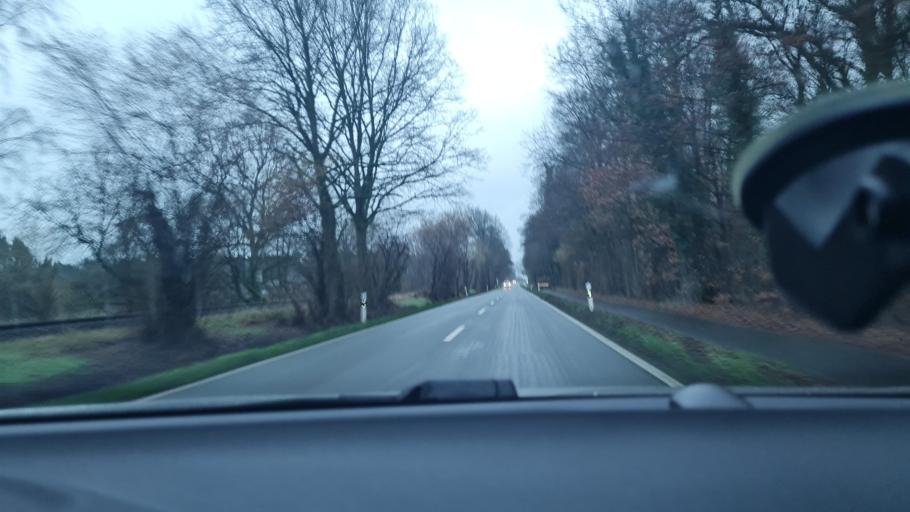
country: DE
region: North Rhine-Westphalia
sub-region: Regierungsbezirk Munster
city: Heiden
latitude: 51.8065
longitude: 6.9075
